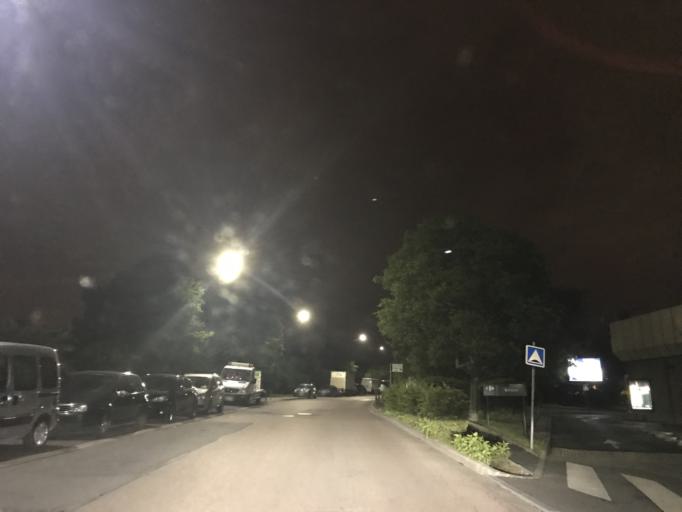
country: FR
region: Ile-de-France
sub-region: Departement des Yvelines
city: Sartrouville
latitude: 48.9461
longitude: 2.1946
